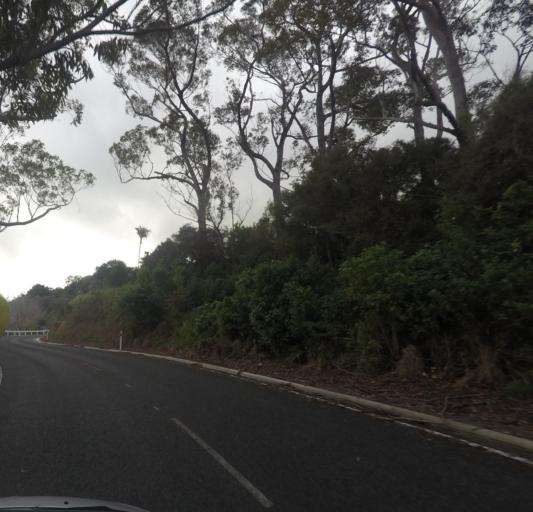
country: NZ
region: Auckland
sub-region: Auckland
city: Warkworth
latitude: -36.3758
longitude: 174.8127
